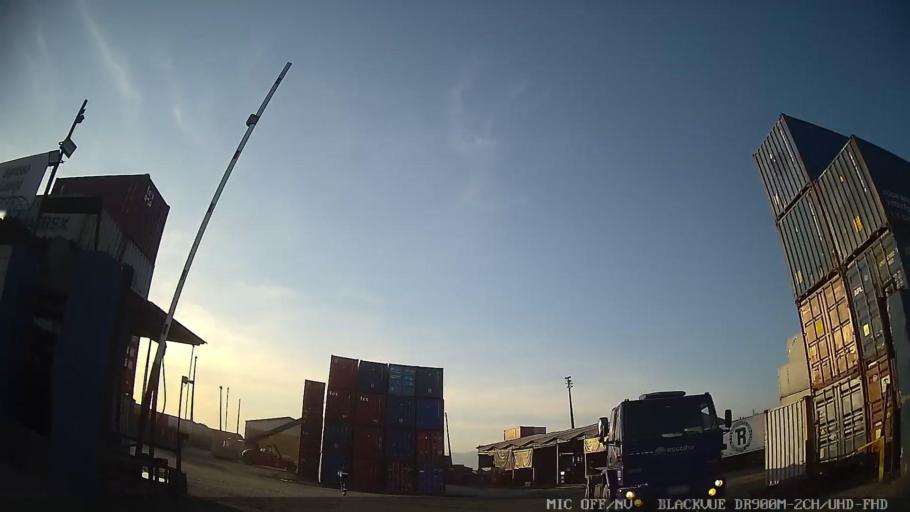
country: BR
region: Sao Paulo
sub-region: Guaruja
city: Guaruja
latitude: -23.9731
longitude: -46.2666
